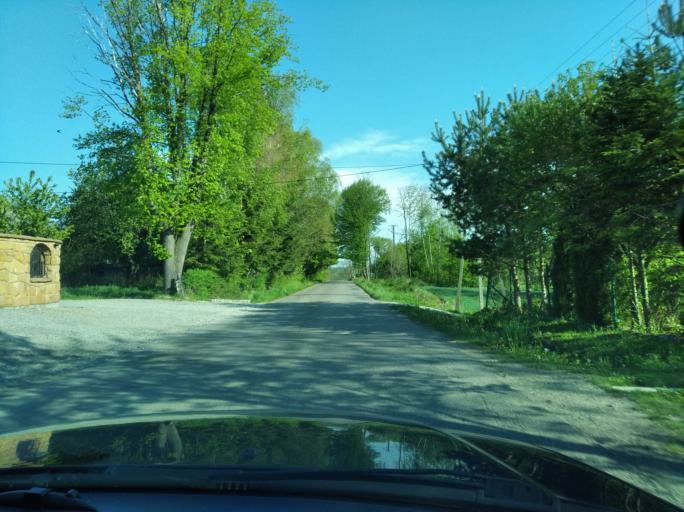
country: PL
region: Subcarpathian Voivodeship
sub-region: Powiat jaroslawski
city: Pruchnik
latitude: 49.8986
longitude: 22.5518
